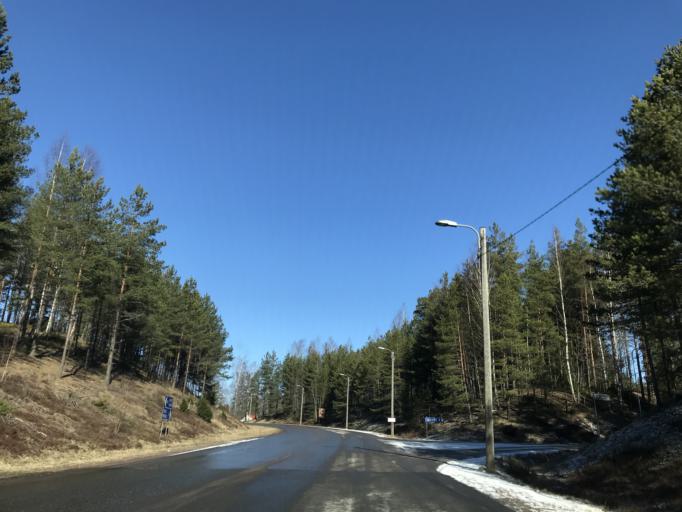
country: FI
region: Uusimaa
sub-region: Raaseporin
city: Karis
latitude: 60.0723
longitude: 23.6930
